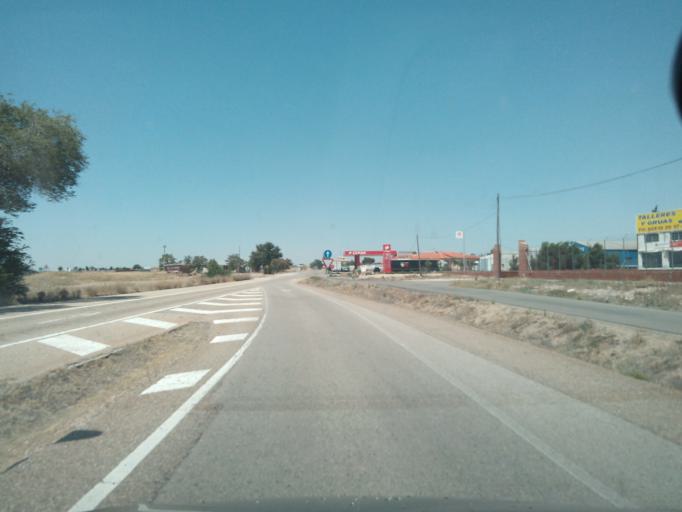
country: ES
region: Castille-La Mancha
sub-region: Province of Toledo
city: Tembleque
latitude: 39.7770
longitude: -3.4785
